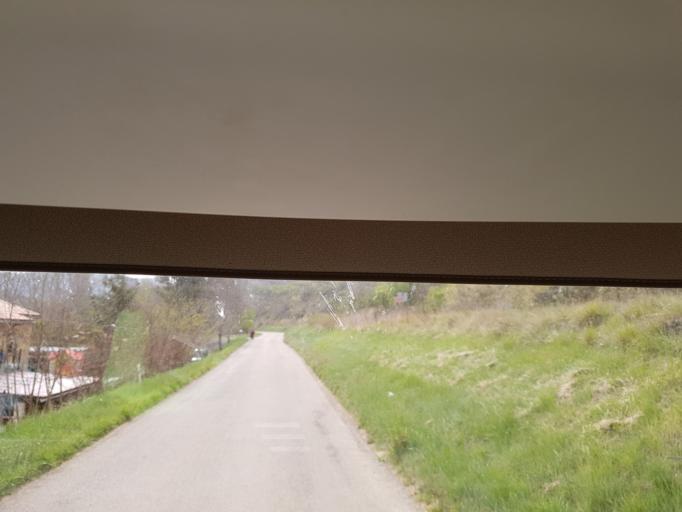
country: FR
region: Languedoc-Roussillon
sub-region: Departement de l'Aude
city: Esperaza
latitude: 42.9152
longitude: 2.2007
